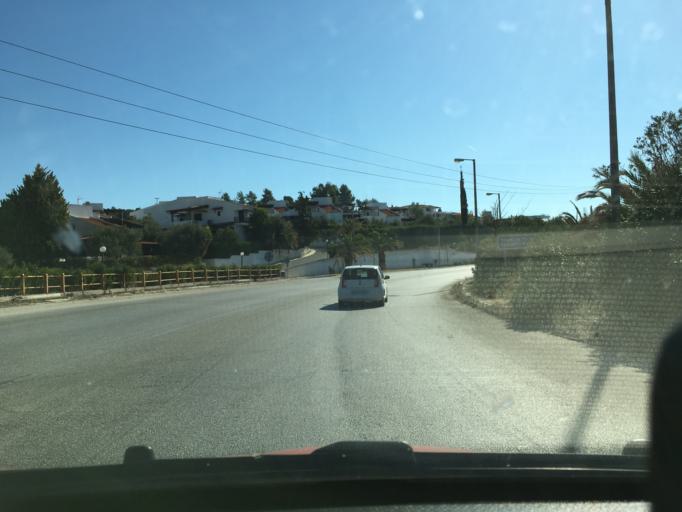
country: GR
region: Central Macedonia
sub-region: Nomos Chalkidikis
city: Ormylia
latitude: 40.2643
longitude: 23.4709
